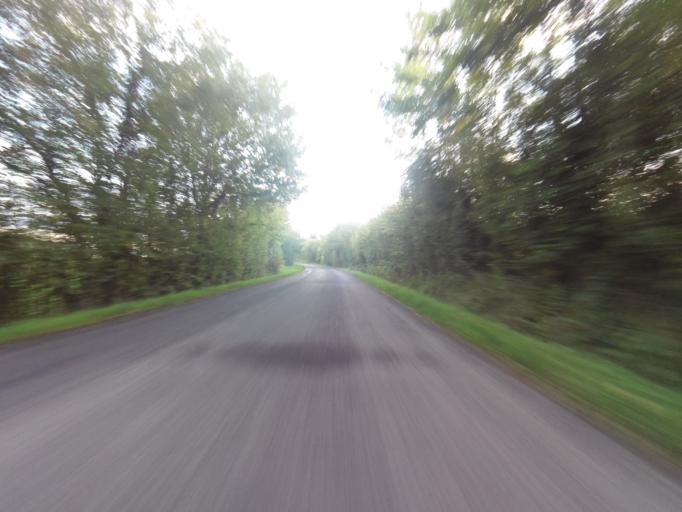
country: FR
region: Lower Normandy
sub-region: Departement de l'Orne
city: Vimoutiers
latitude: 48.9220
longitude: 0.2642
